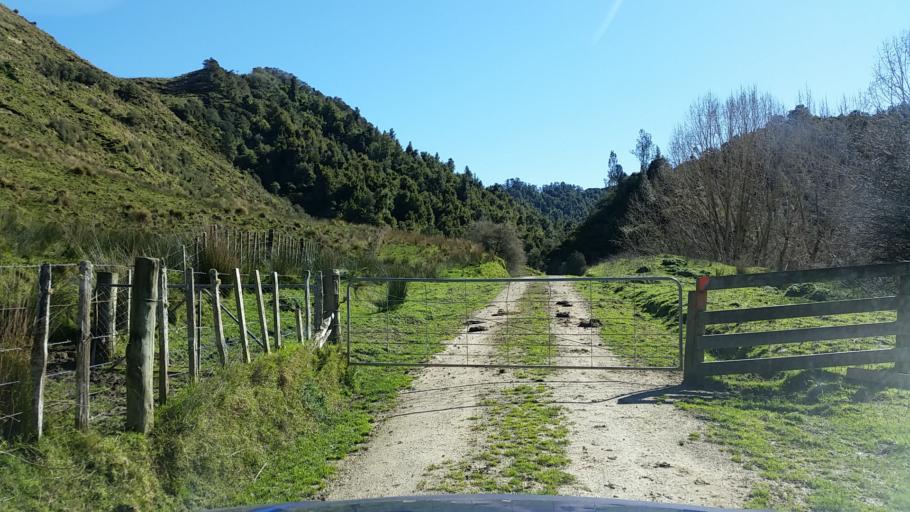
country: NZ
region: Manawatu-Wanganui
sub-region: Wanganui District
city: Wanganui
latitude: -39.6696
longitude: 174.8576
